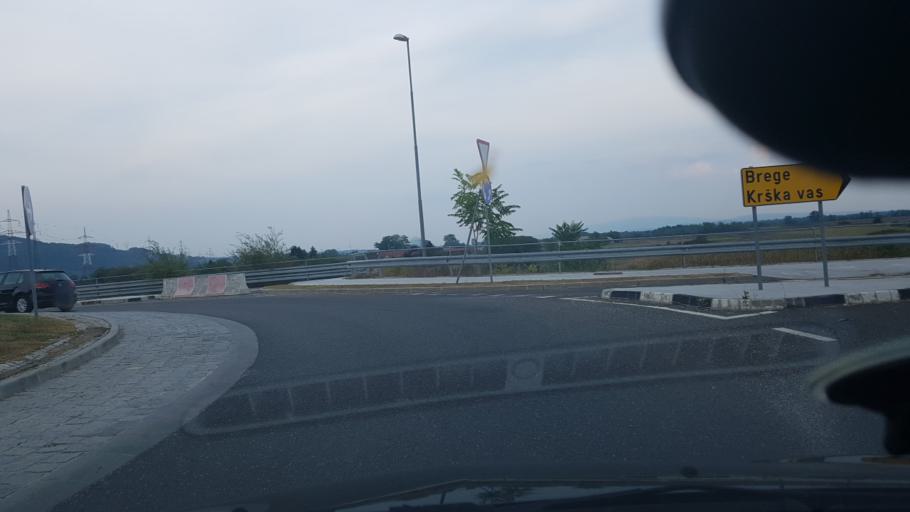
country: SI
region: Krsko
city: Leskovec pri Krskem
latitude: 45.9339
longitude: 15.4843
